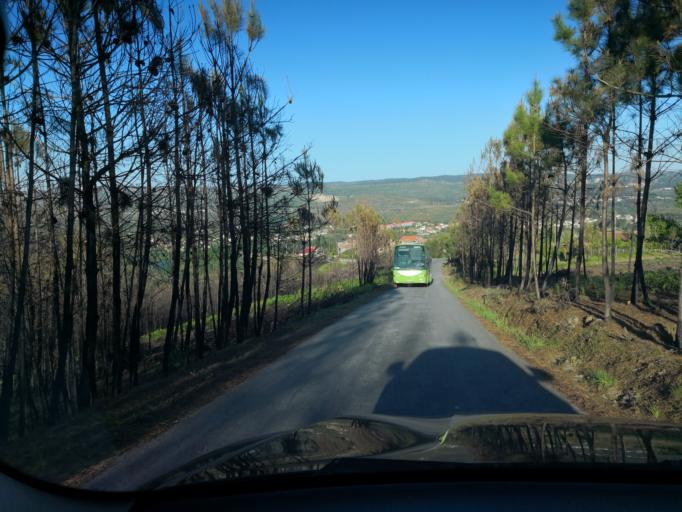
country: PT
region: Vila Real
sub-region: Vila Real
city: Vila Real
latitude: 41.3465
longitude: -7.7444
